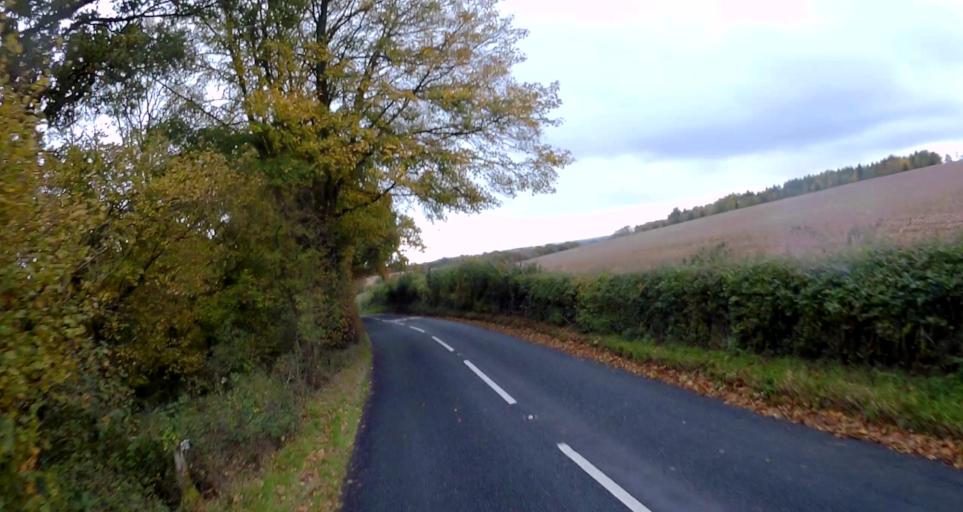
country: GB
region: England
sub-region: Hampshire
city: Four Marks
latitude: 51.1180
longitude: -1.1569
